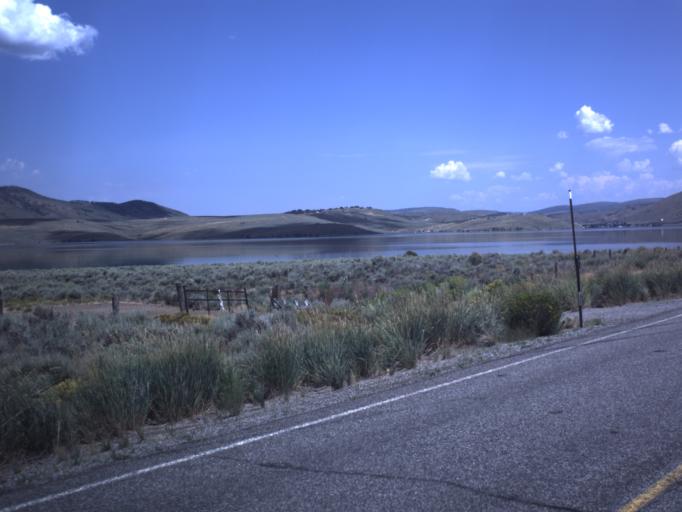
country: US
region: Utah
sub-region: Carbon County
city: Helper
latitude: 39.7623
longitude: -111.1432
